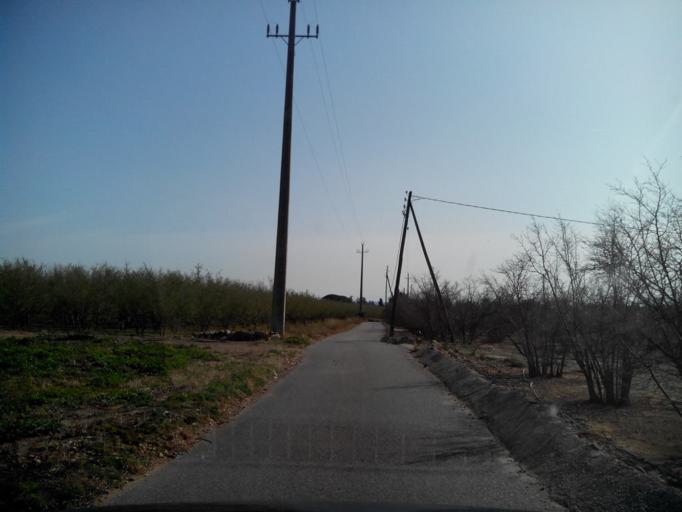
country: ES
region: Catalonia
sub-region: Provincia de Tarragona
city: La Selva
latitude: 41.2119
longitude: 1.1693
